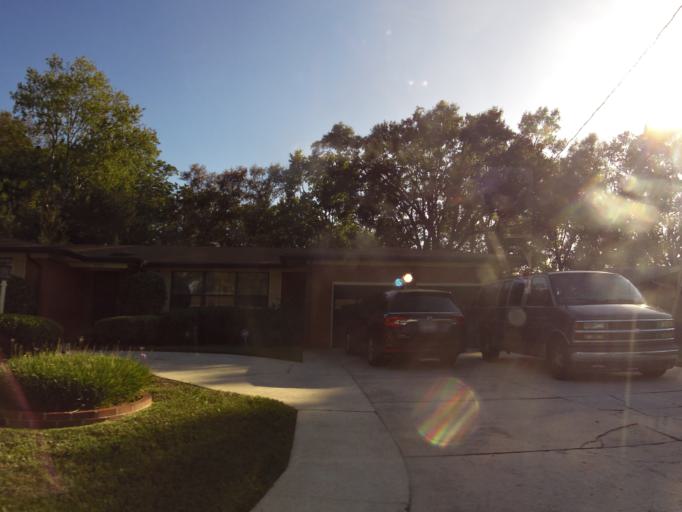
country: US
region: Florida
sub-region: Duval County
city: Jacksonville
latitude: 30.2518
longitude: -81.6305
